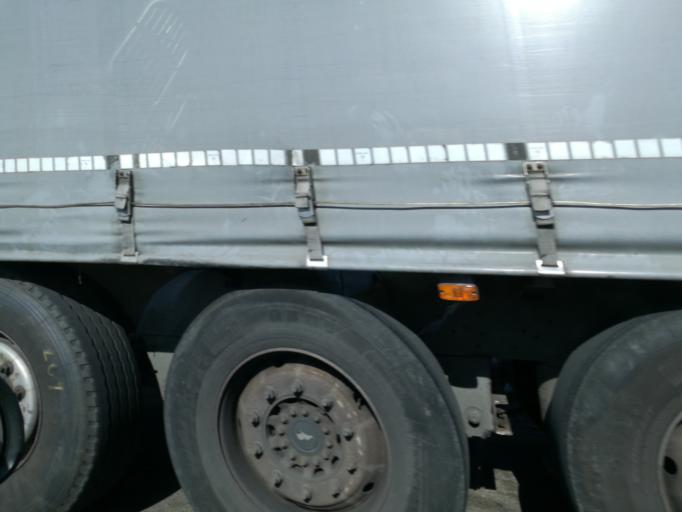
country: RO
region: Ilfov
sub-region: Comuna Chiajna
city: Chiajna
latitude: 44.4406
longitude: 25.9592
